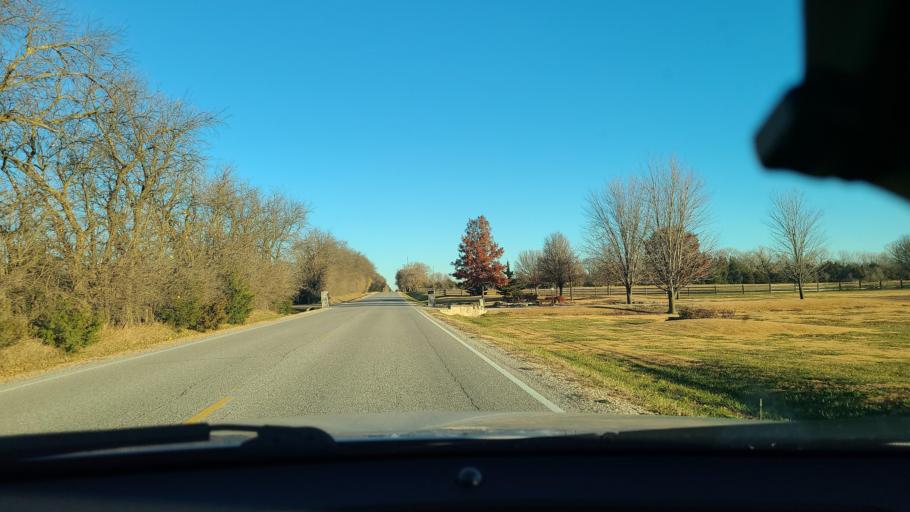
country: US
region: Kansas
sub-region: Sedgwick County
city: Park City
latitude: 37.8476
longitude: -97.3174
